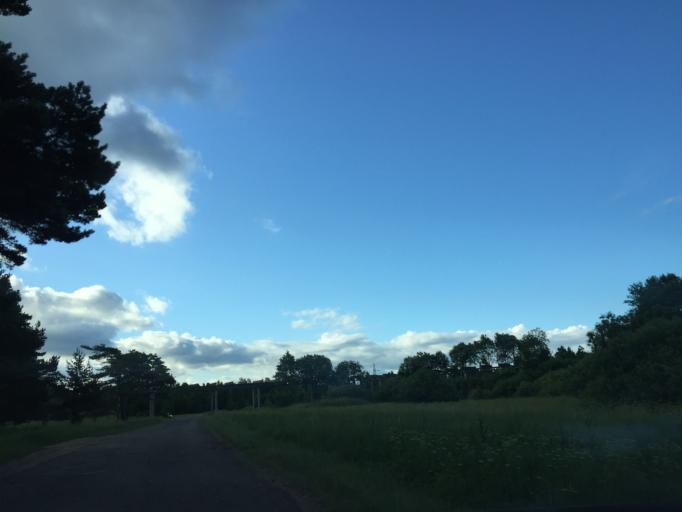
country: LV
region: Ventspils
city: Ventspils
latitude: 57.4107
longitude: 21.6160
